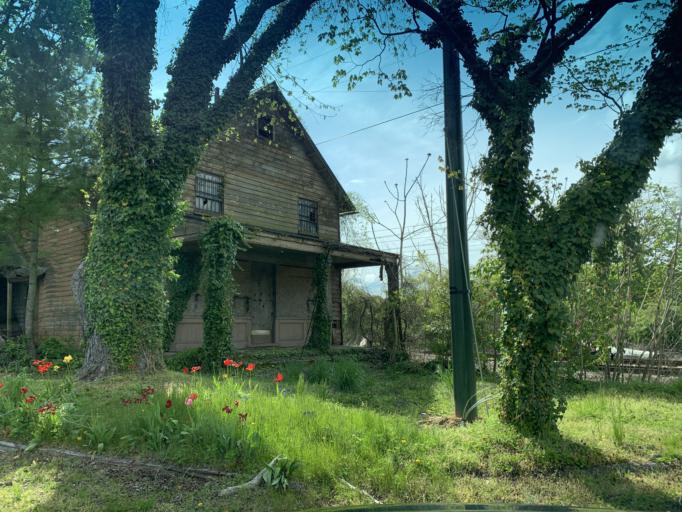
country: US
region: Maryland
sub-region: Harford County
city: Perryman
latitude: 39.4654
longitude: -76.2005
